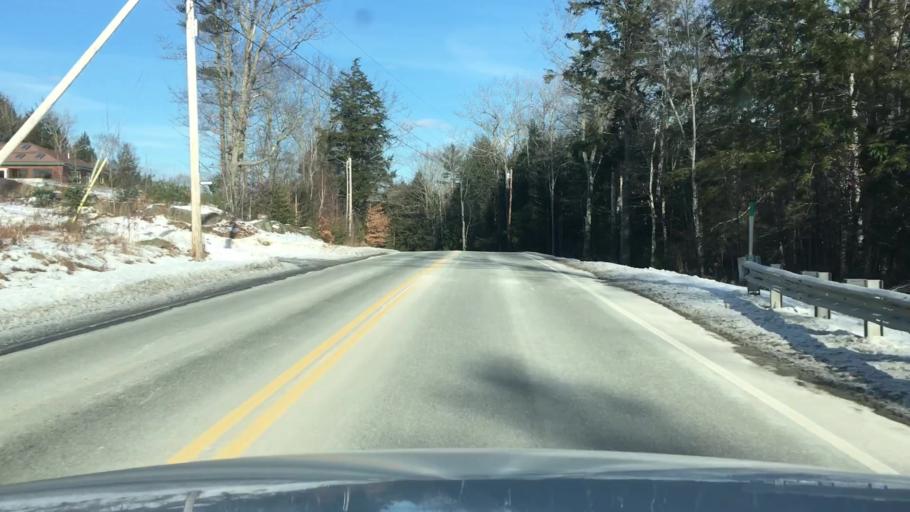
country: US
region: Maine
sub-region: Hancock County
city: Dedham
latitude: 44.6334
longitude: -68.7004
